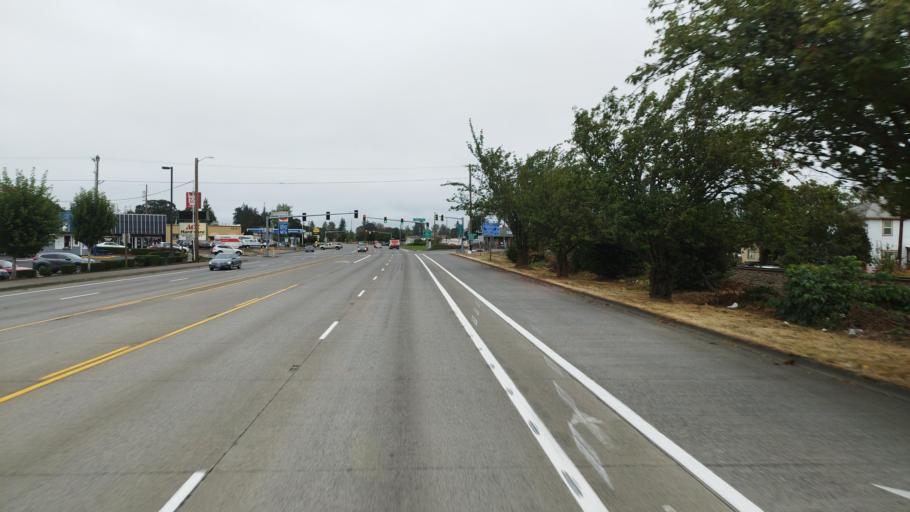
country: US
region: Oregon
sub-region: Columbia County
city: Saint Helens
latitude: 45.8580
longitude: -122.8221
